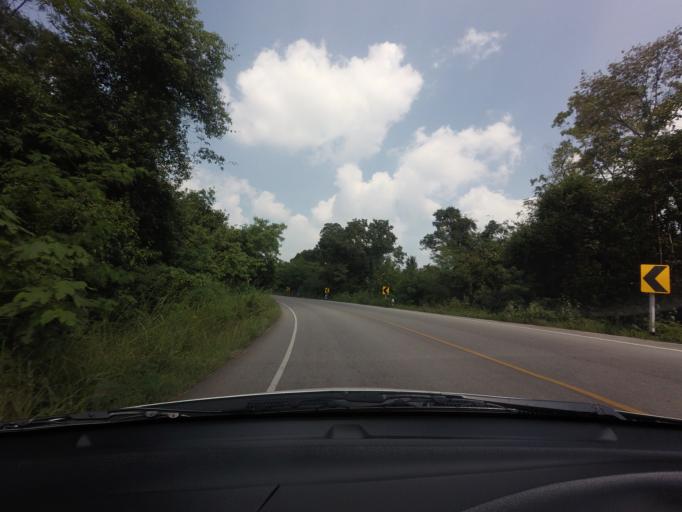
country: TH
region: Nakhon Ratchasima
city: Pak Chong
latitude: 14.6087
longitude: 101.5767
